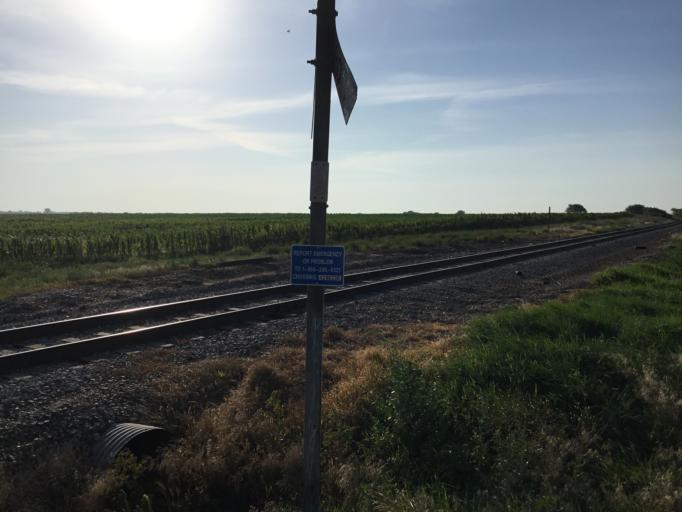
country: US
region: Kansas
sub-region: Sedgwick County
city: Cheney
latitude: 37.4970
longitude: -97.9355
